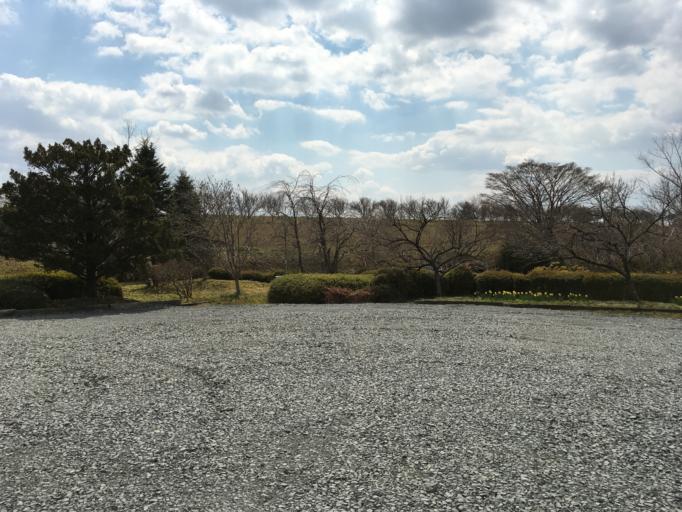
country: JP
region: Iwate
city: Ichinoseki
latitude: 38.8169
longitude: 141.2736
